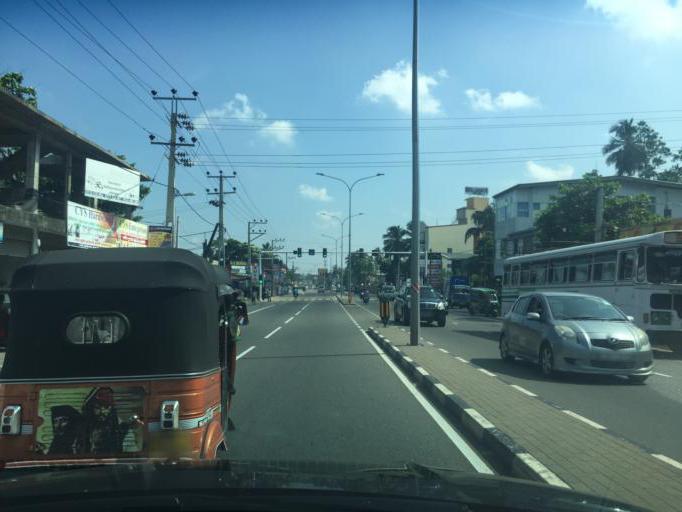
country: LK
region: Western
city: Maharagama
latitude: 6.8252
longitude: 79.9132
